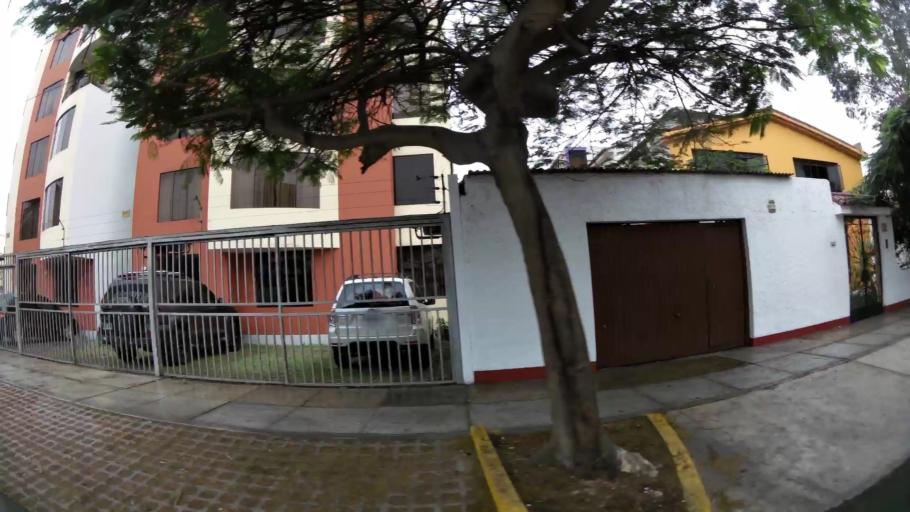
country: PE
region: Lima
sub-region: Lima
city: Surco
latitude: -12.1371
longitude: -77.0041
